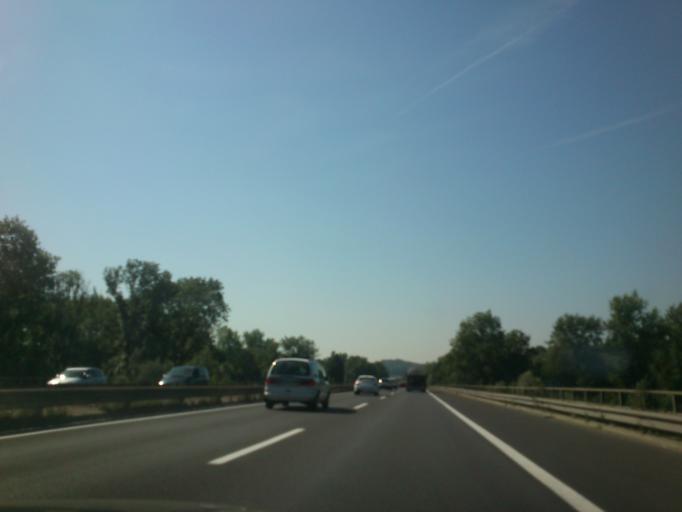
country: AT
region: Upper Austria
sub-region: Politischer Bezirk Linz-Land
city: Ansfelden
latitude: 48.2362
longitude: 14.2976
